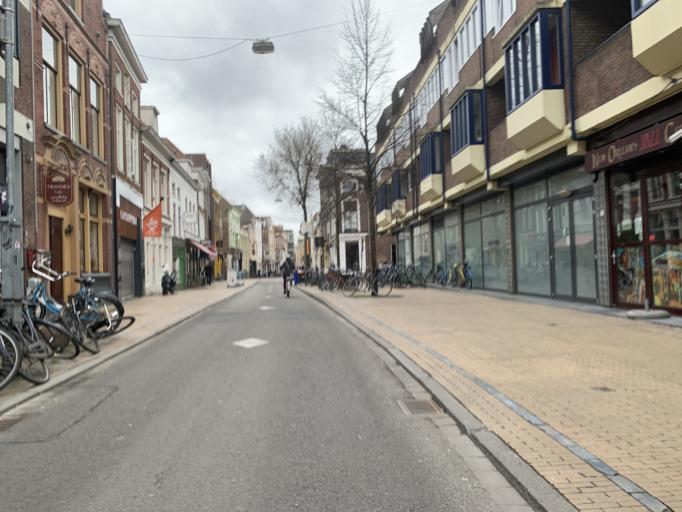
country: NL
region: Groningen
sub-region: Gemeente Groningen
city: Groningen
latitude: 53.2176
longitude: 6.5682
